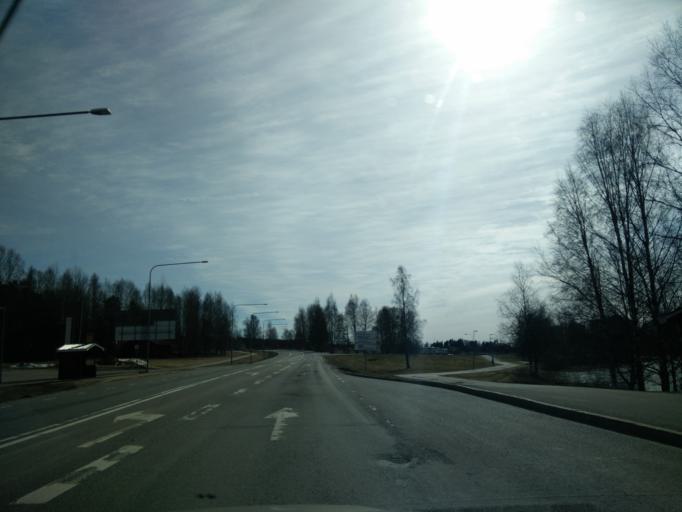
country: SE
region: Vaermland
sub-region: Hagfors Kommun
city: Hagfors
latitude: 60.0420
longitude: 13.7033
